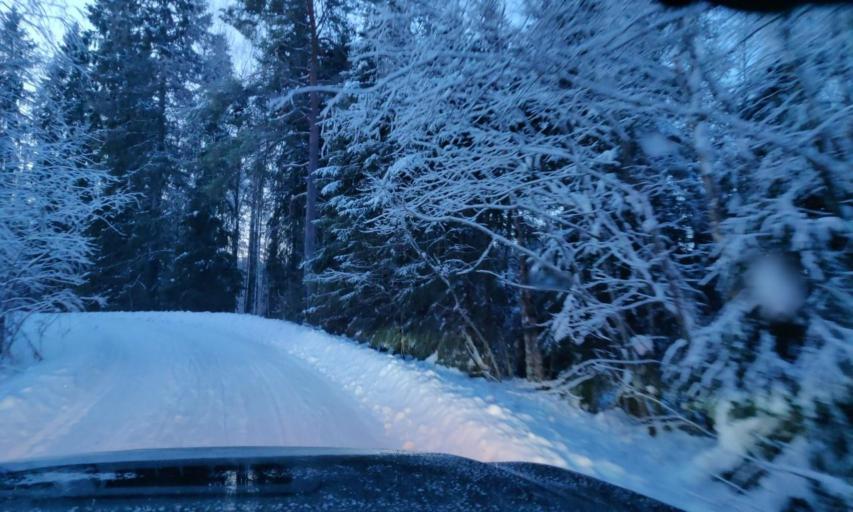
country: FI
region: Kainuu
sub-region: Kajaani
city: Paltamo
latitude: 64.3007
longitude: 28.0033
